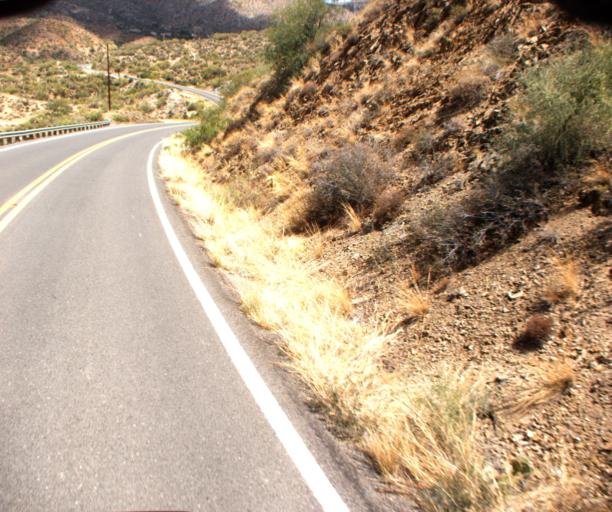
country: US
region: Arizona
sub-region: Pinal County
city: Superior
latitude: 33.1807
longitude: -111.0415
